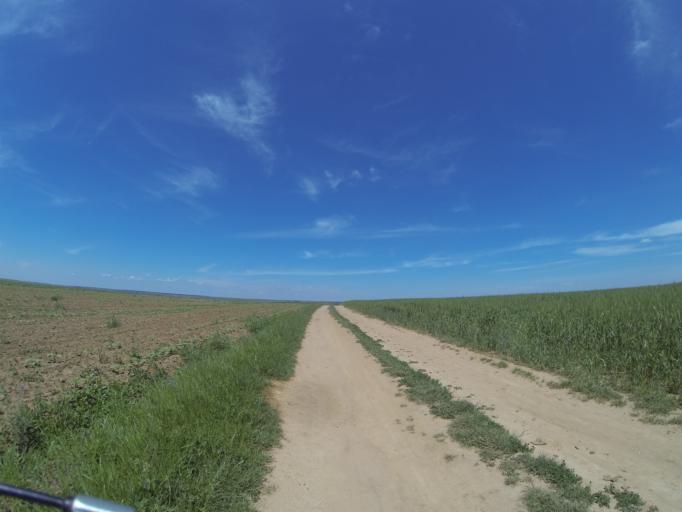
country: RO
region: Dolj
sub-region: Comuna Teslui
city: Teslui
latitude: 44.1866
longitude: 24.1722
